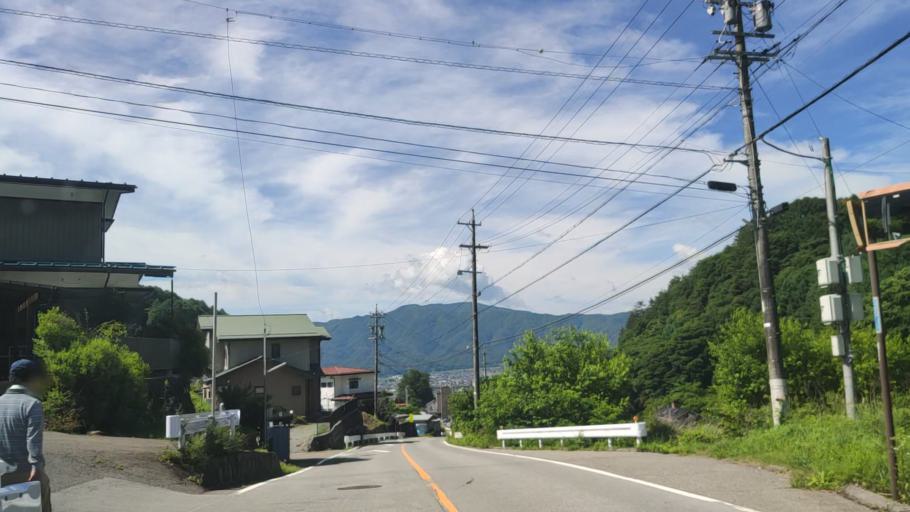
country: JP
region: Nagano
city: Suwa
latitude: 36.0542
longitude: 138.1289
